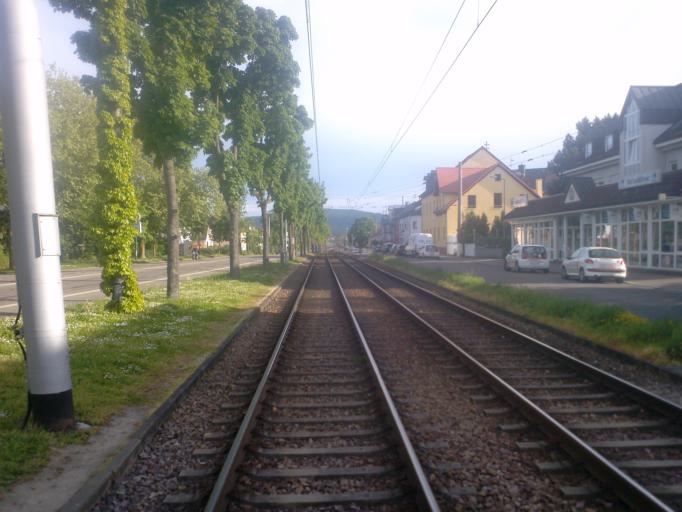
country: DE
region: Baden-Wuerttemberg
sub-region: Karlsruhe Region
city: Ettlingen
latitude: 48.9704
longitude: 8.4042
